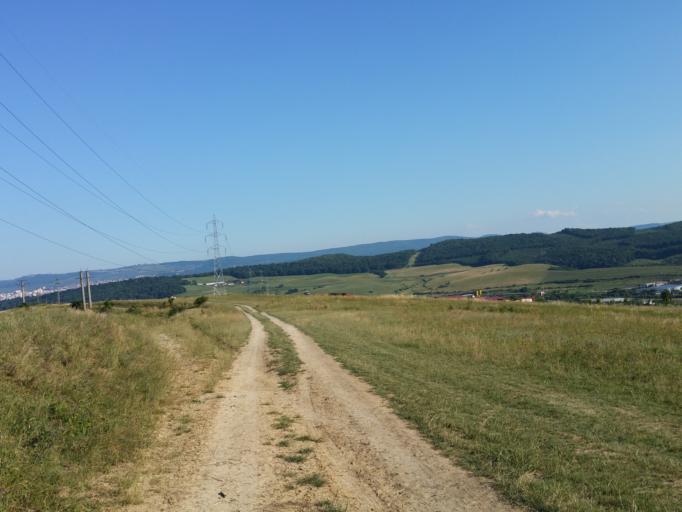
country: RO
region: Cluj
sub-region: Comuna Baciu
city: Baciu
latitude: 46.7954
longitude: 23.5310
